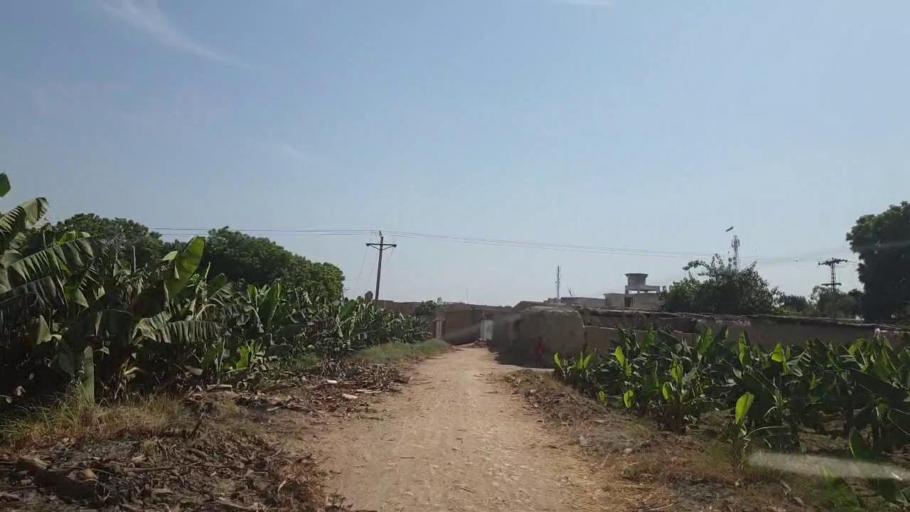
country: PK
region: Sindh
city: Tando Allahyar
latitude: 25.3900
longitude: 68.6736
